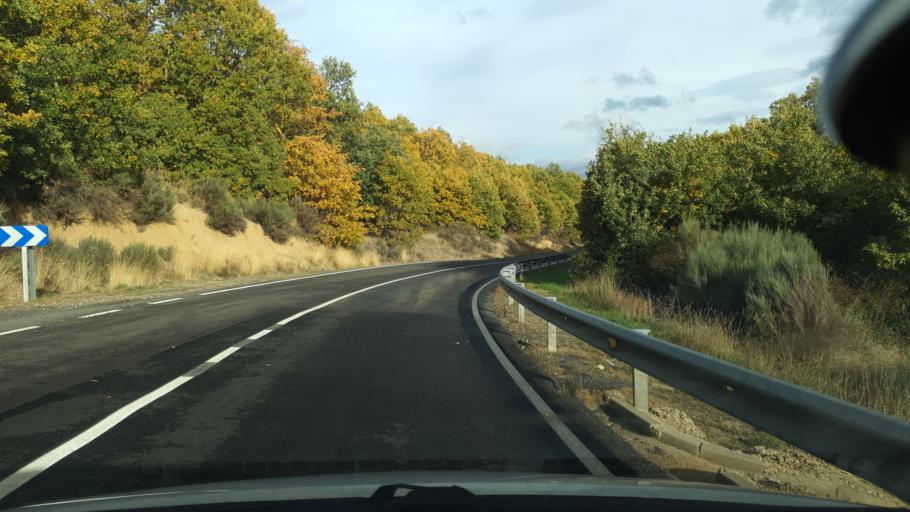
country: ES
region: Castille and Leon
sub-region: Provincia de Avila
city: Hoyocasero
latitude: 40.3947
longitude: -4.9945
